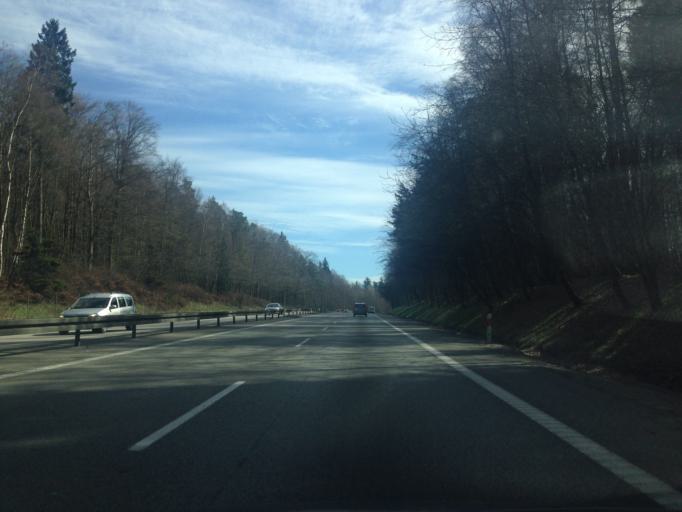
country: PL
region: Pomeranian Voivodeship
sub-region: Gdynia
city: Wielki Kack
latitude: 54.4552
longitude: 18.4910
